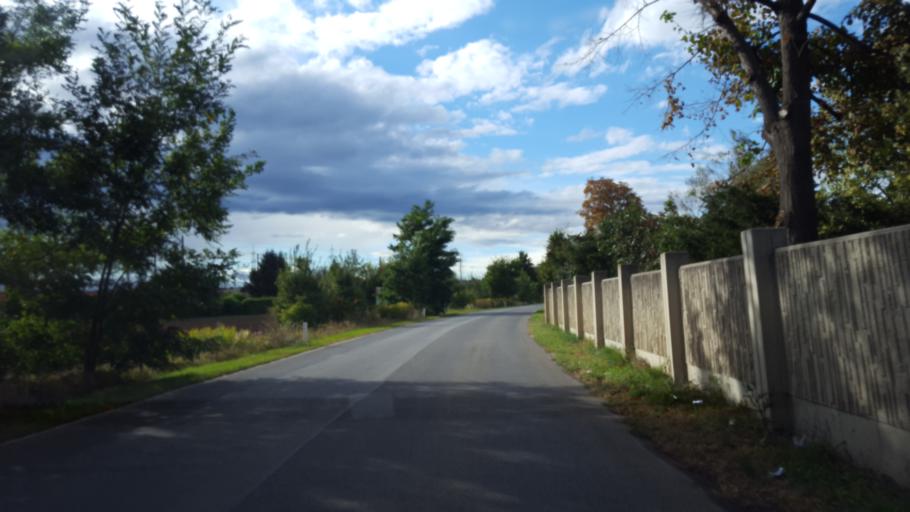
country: AT
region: Lower Austria
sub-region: Politischer Bezirk Wien-Umgebung
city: Schwechat
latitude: 48.1418
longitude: 16.4357
